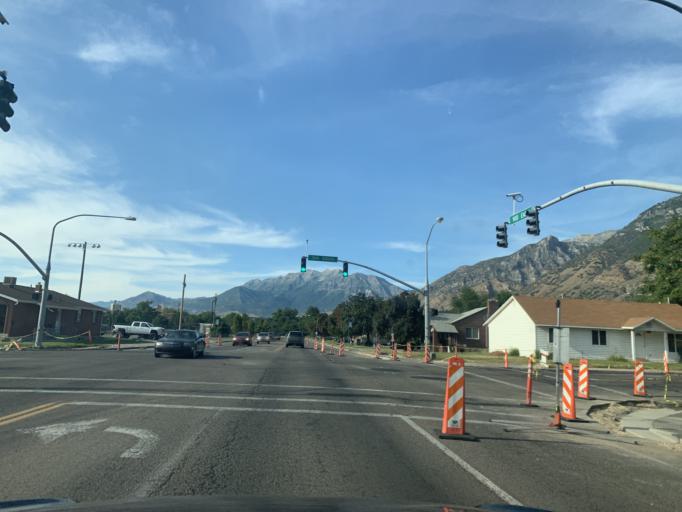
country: US
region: Utah
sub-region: Utah County
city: Provo
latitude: 40.2295
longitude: -111.6427
